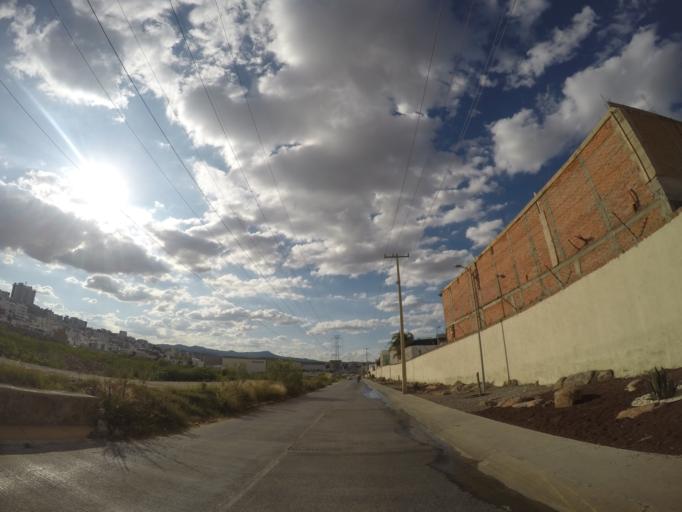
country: MX
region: San Luis Potosi
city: Escalerillas
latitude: 22.1239
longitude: -101.0254
